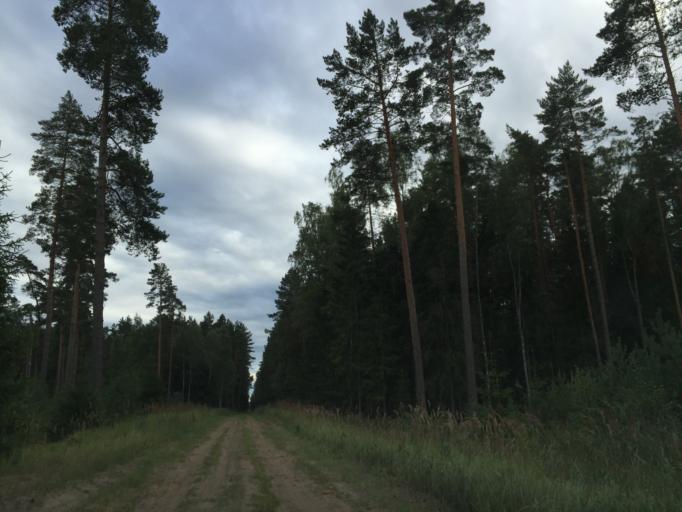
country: LV
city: Tireli
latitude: 56.8452
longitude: 23.6848
